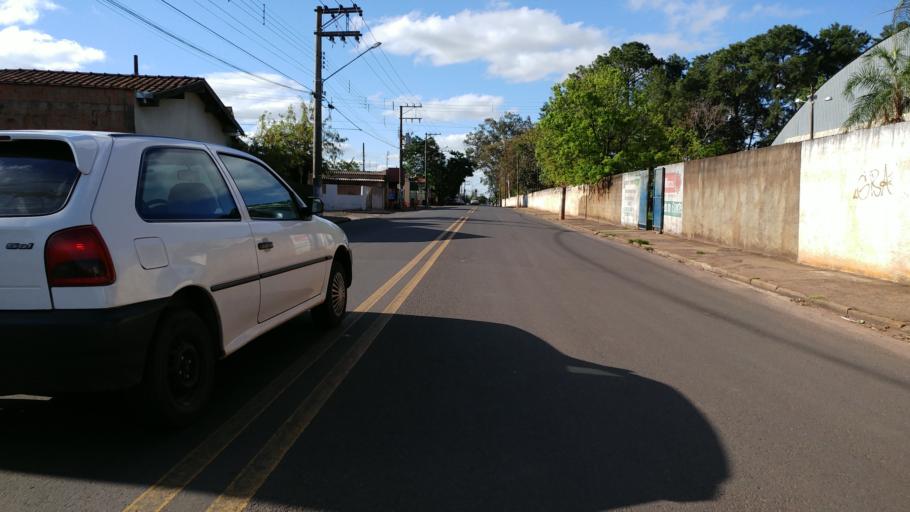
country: BR
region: Sao Paulo
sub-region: Paraguacu Paulista
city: Paraguacu Paulista
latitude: -22.4295
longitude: -50.5786
